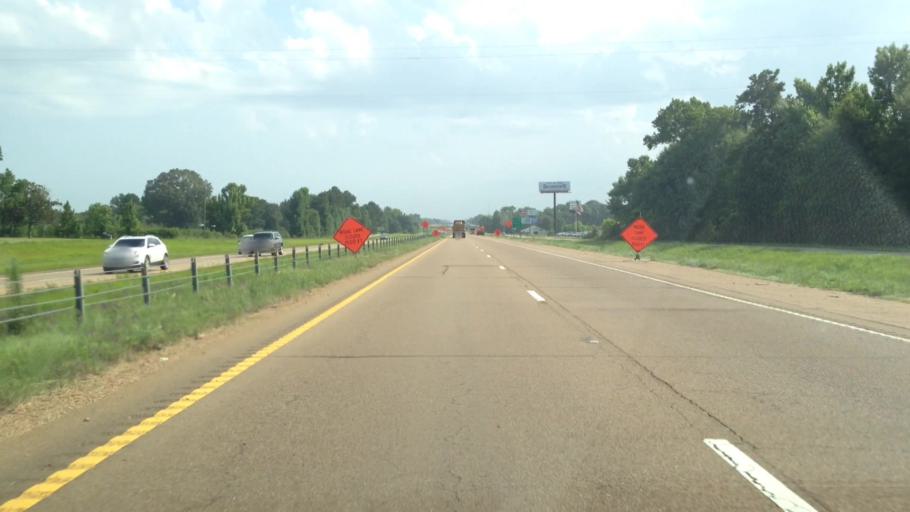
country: US
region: Mississippi
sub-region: Hinds County
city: Terry
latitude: 32.0834
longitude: -90.3118
